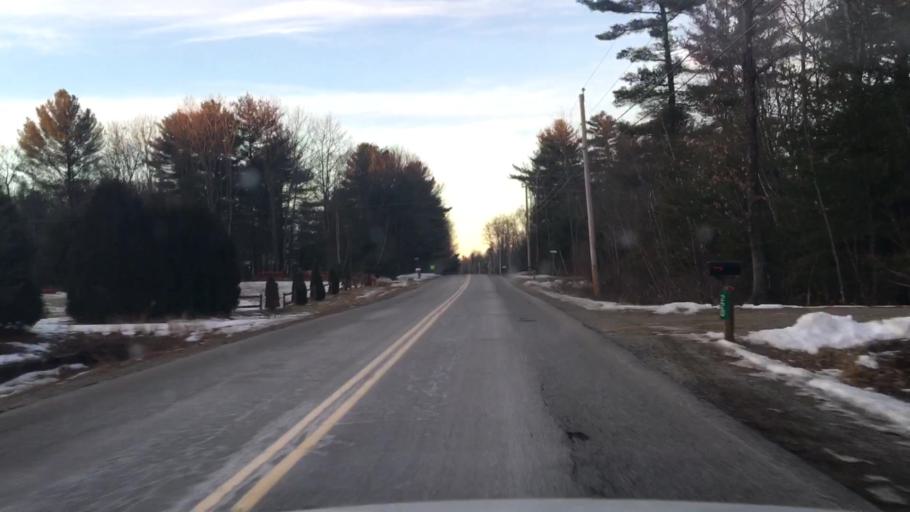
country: US
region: Maine
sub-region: York County
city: Lebanon
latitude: 43.3484
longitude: -70.8663
